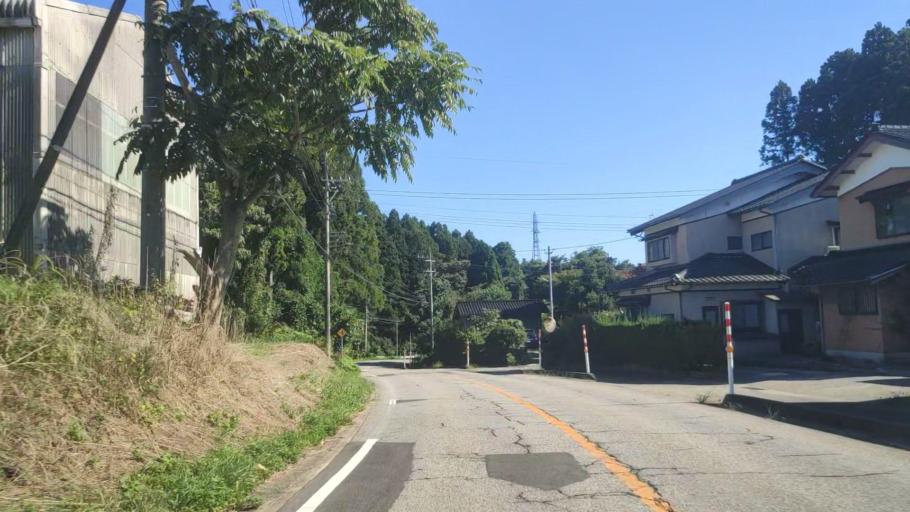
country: JP
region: Ishikawa
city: Nanao
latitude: 37.3436
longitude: 137.2285
